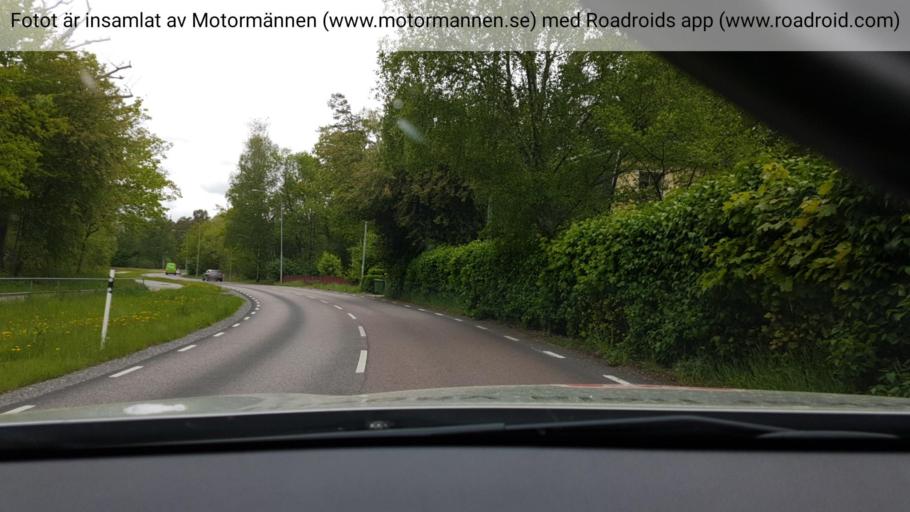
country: SE
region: Stockholm
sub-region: Lidingo
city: Brevik
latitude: 59.3487
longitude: 18.1741
